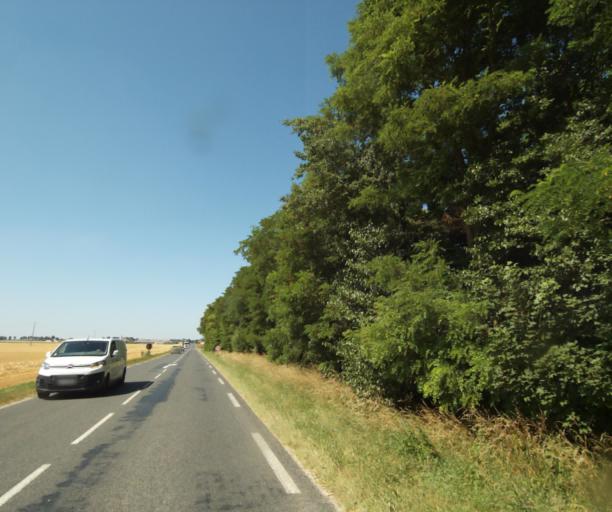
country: FR
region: Ile-de-France
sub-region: Departement de Seine-et-Marne
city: La Chapelle-la-Reine
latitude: 48.3006
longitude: 2.5737
